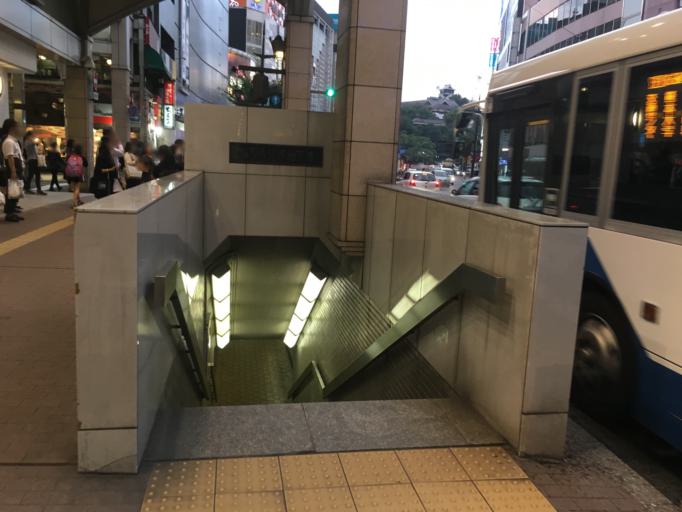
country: JP
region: Kumamoto
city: Kumamoto
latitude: 32.8031
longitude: 130.7109
